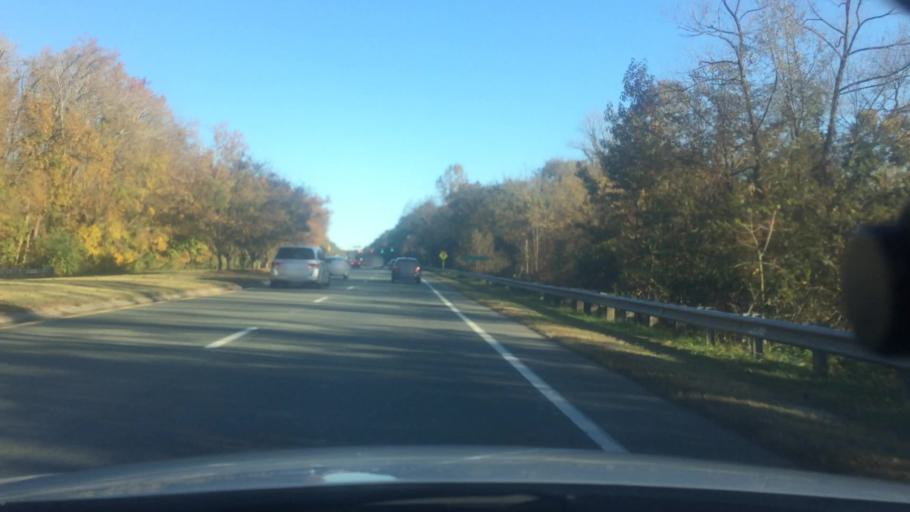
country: US
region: North Carolina
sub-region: Orange County
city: Chapel Hill
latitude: 35.9226
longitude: -79.0253
